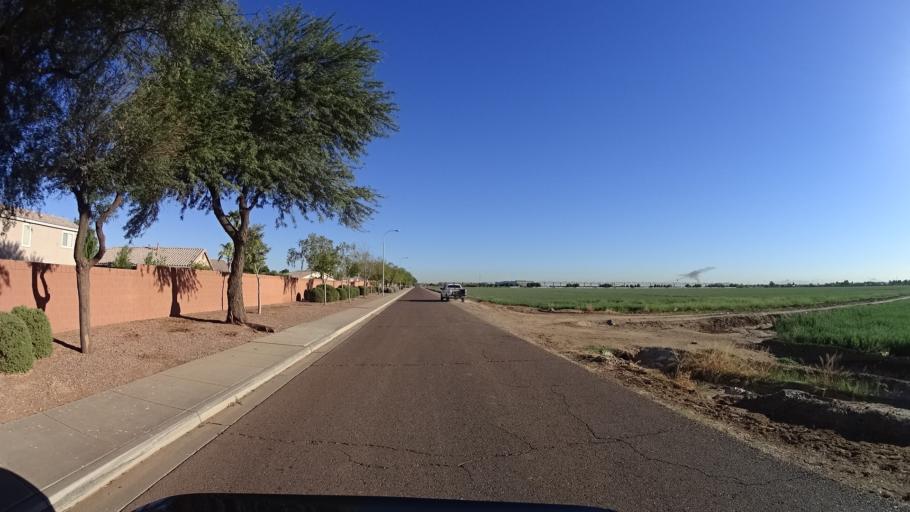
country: US
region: Arizona
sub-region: Maricopa County
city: Tolleson
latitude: 33.4258
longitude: -112.2126
